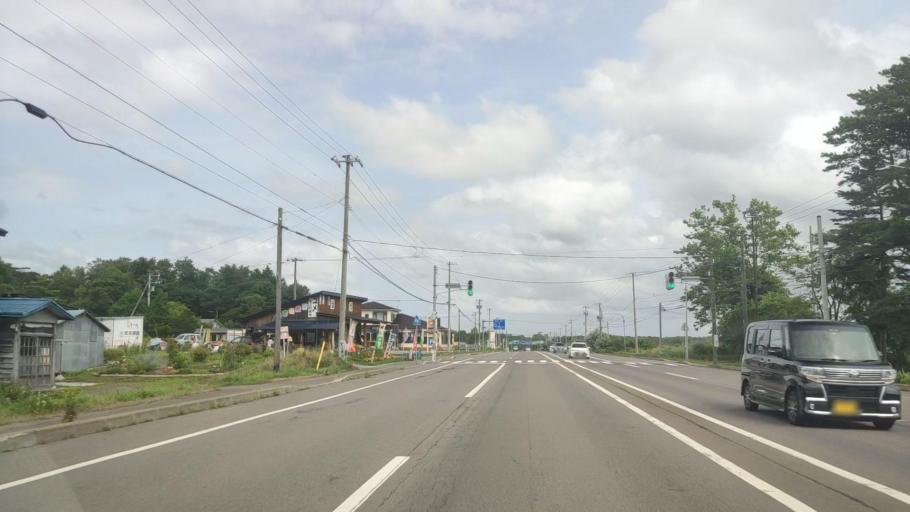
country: JP
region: Hokkaido
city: Nanae
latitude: 42.0031
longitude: 140.6334
